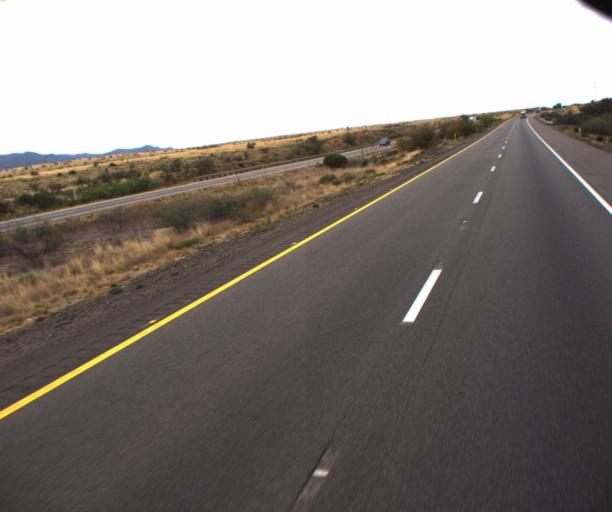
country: US
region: Arizona
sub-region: Cochise County
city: Willcox
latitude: 32.0959
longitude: -110.0346
